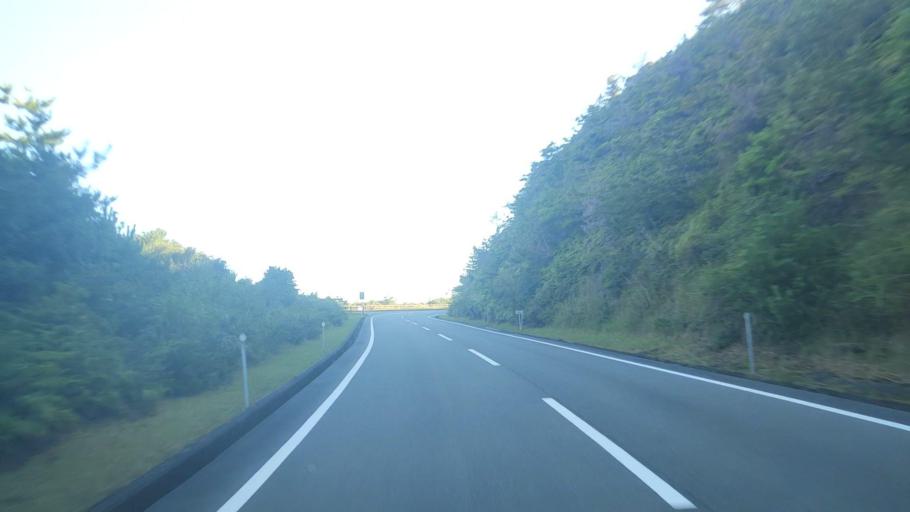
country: JP
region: Mie
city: Toba
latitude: 34.4170
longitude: 136.9130
